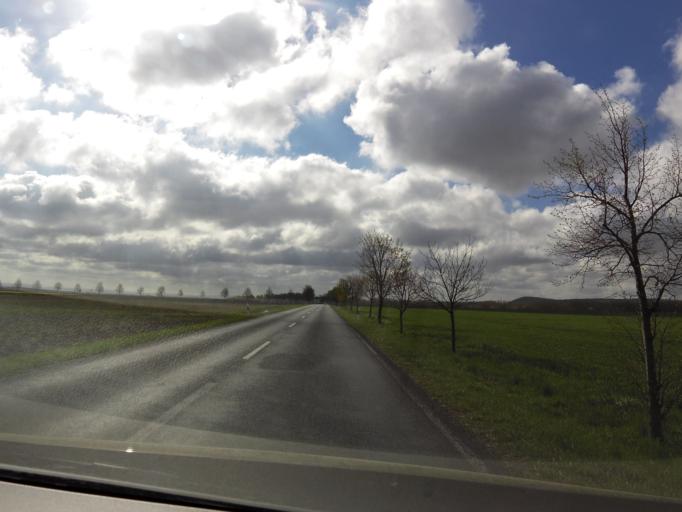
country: DE
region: Thuringia
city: Seebergen
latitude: 50.9172
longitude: 10.8077
